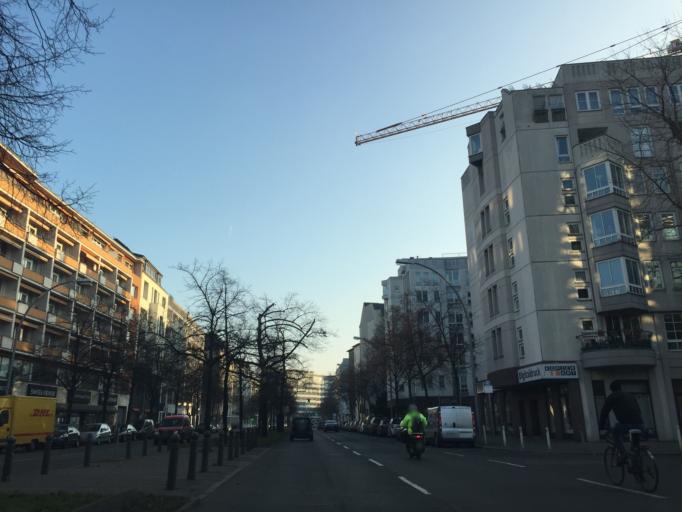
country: DE
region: Berlin
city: Wilmersdorf Bezirk
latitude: 52.5001
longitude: 13.3268
